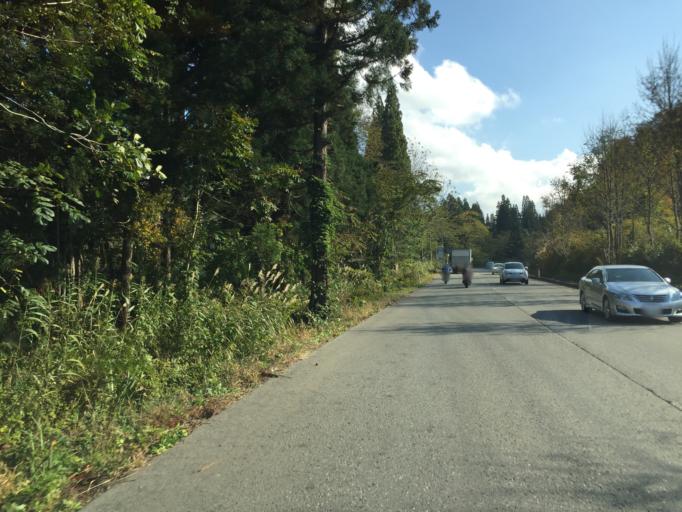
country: JP
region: Yamagata
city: Yonezawa
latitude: 37.8520
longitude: 139.9933
